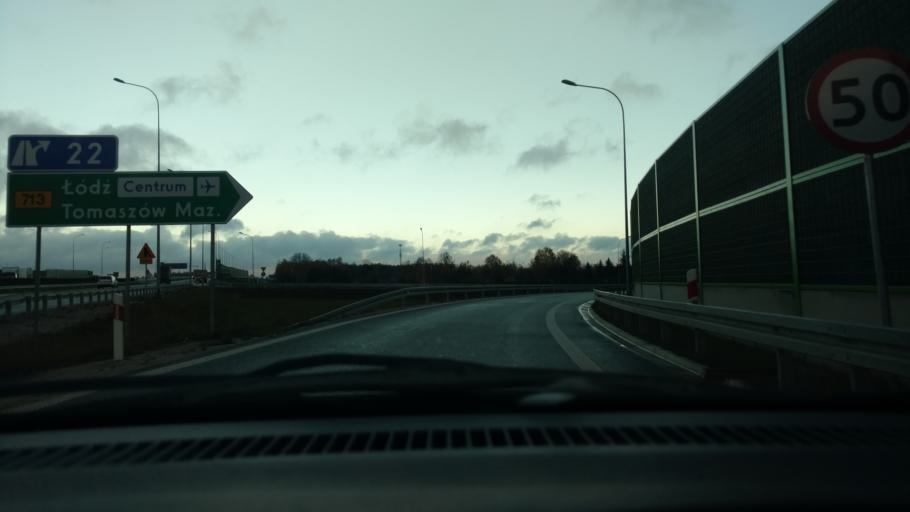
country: PL
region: Lodz Voivodeship
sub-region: Powiat lodzki wschodni
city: Andrespol
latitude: 51.7445
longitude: 19.5987
